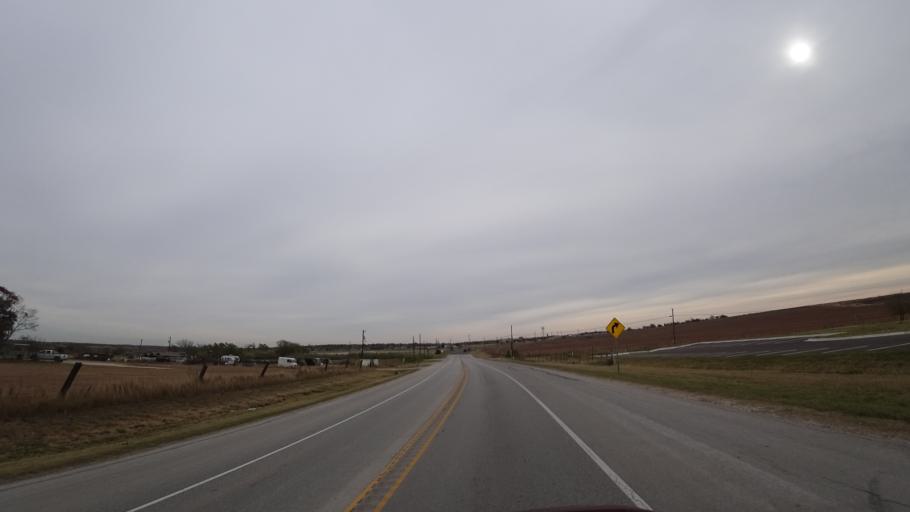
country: US
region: Texas
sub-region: Travis County
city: Garfield
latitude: 30.1029
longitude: -97.6135
